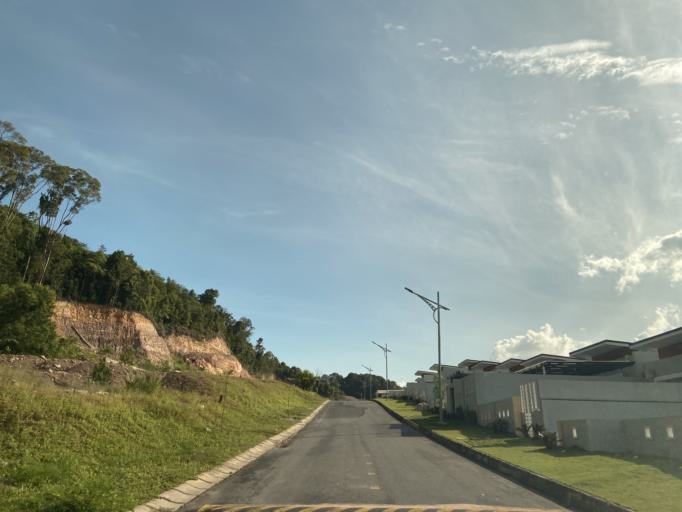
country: SG
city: Singapore
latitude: 1.0937
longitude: 104.0268
